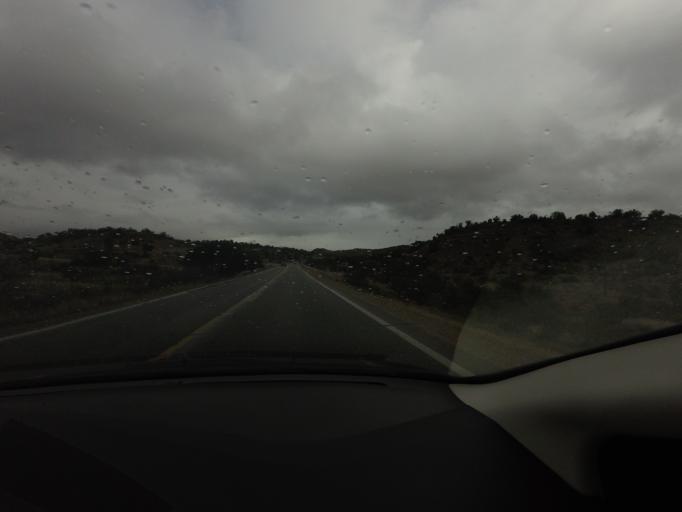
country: US
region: Arizona
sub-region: Yavapai County
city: Cornville
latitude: 34.7046
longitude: -111.8728
